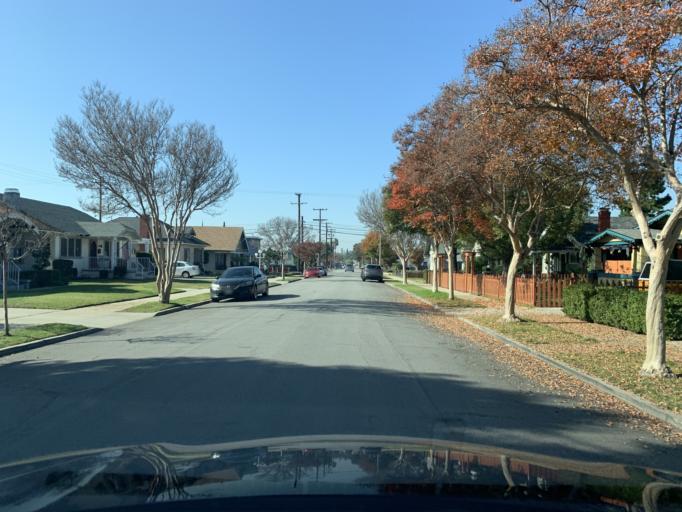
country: US
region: California
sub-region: Los Angeles County
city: Covina
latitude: 34.0885
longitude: -117.8848
